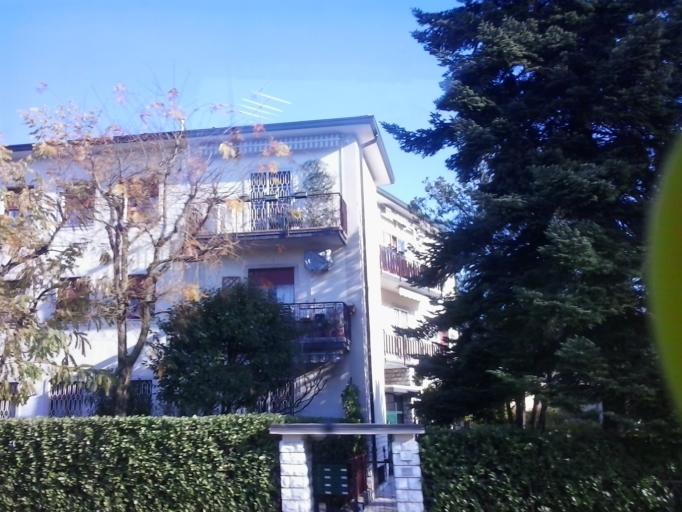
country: IT
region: Lombardy
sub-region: Provincia di Brescia
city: Brescia
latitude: 45.5595
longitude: 10.2338
